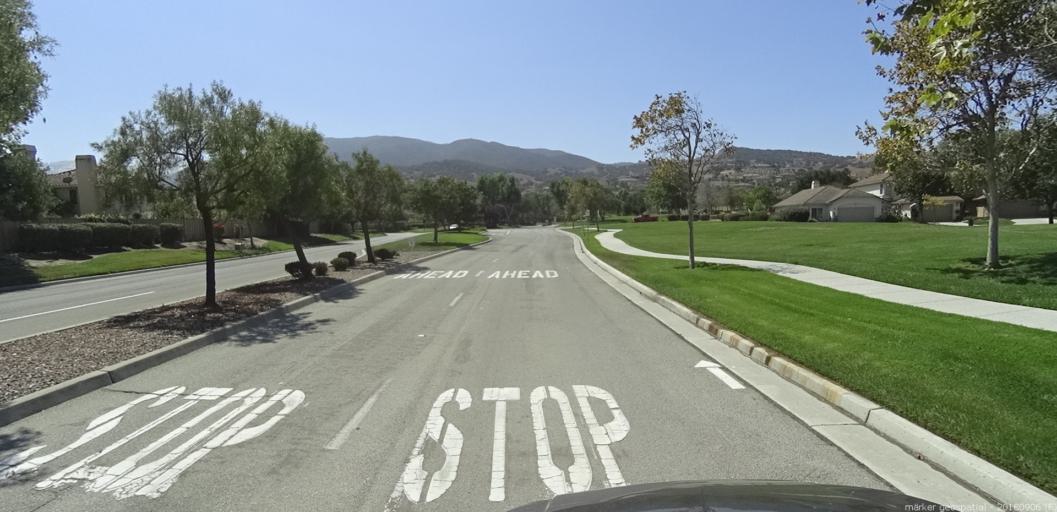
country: US
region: California
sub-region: Monterey County
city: Salinas
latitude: 36.6061
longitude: -121.6449
